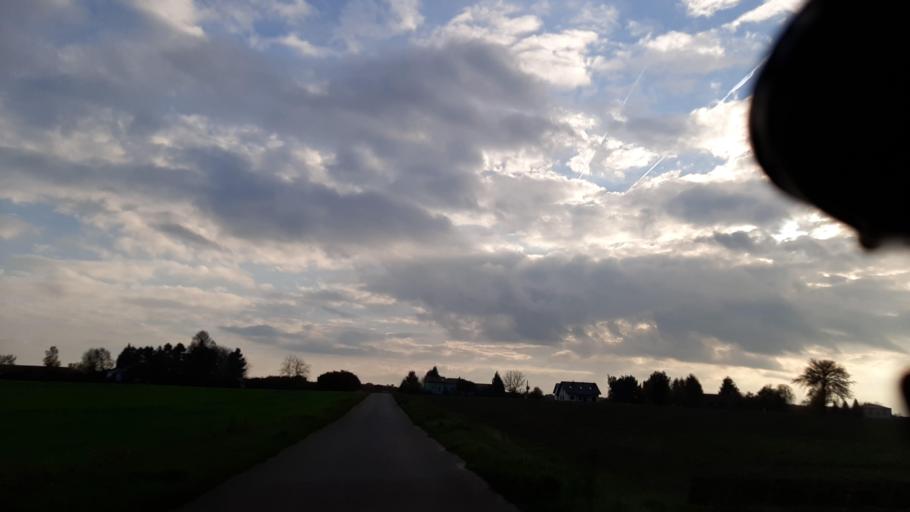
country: PL
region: Lublin Voivodeship
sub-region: Powiat lubelski
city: Garbow
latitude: 51.3405
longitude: 22.3205
